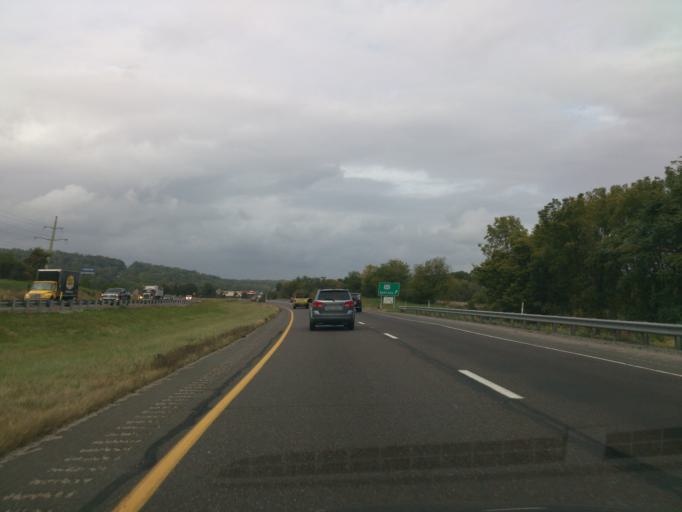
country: US
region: Pennsylvania
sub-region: Lancaster County
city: Ephrata
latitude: 40.1575
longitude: -76.1536
